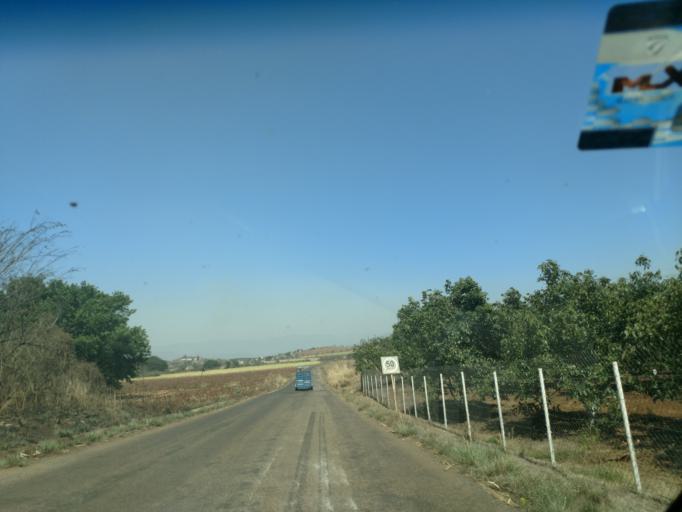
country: MX
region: Nayarit
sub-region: Tepic
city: La Corregidora
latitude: 21.5039
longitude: -104.7257
